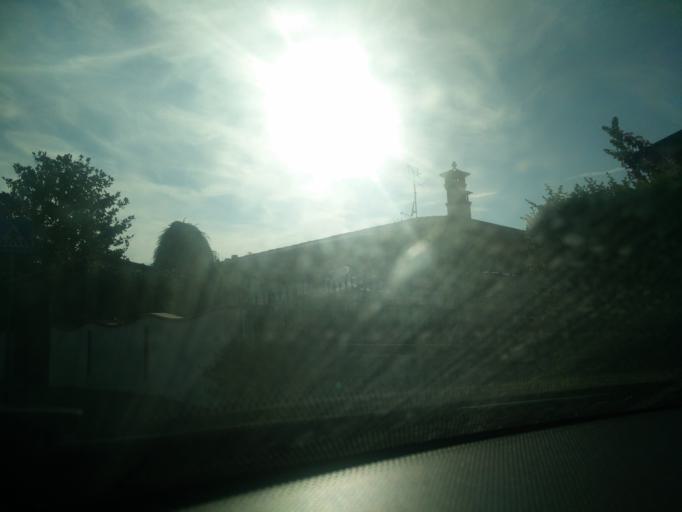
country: IT
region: Tuscany
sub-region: Provincia di Massa-Carrara
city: Massa
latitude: 44.0239
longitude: 10.1230
